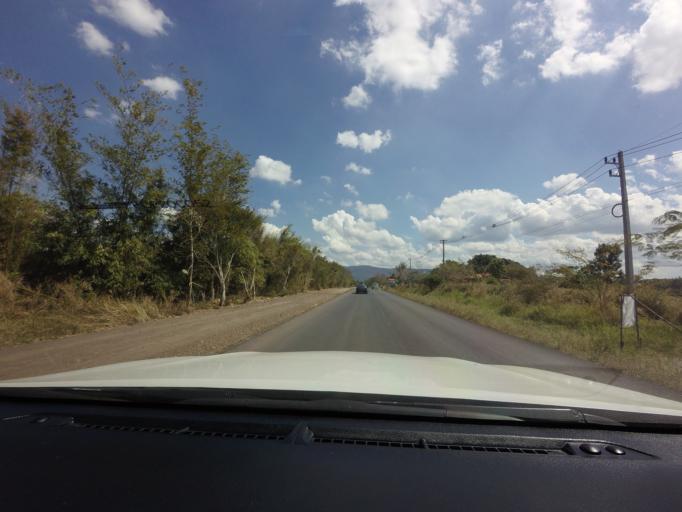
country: TH
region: Nakhon Ratchasima
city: Wang Nam Khiao
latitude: 14.3670
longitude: 101.9060
